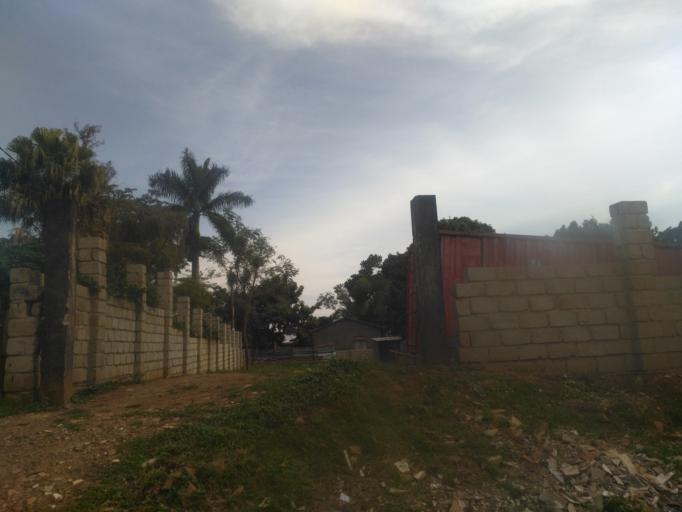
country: UG
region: Central Region
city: Kampala Central Division
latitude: 0.3485
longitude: 32.5969
